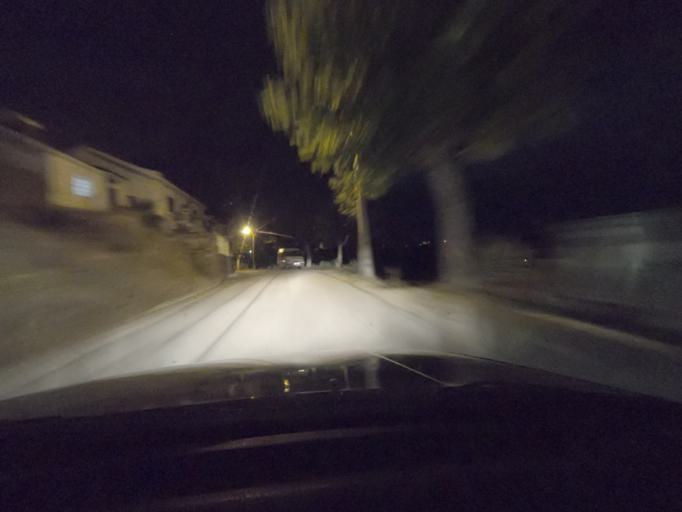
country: PT
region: Vila Real
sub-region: Santa Marta de Penaguiao
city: Santa Marta de Penaguiao
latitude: 41.2266
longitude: -7.8360
